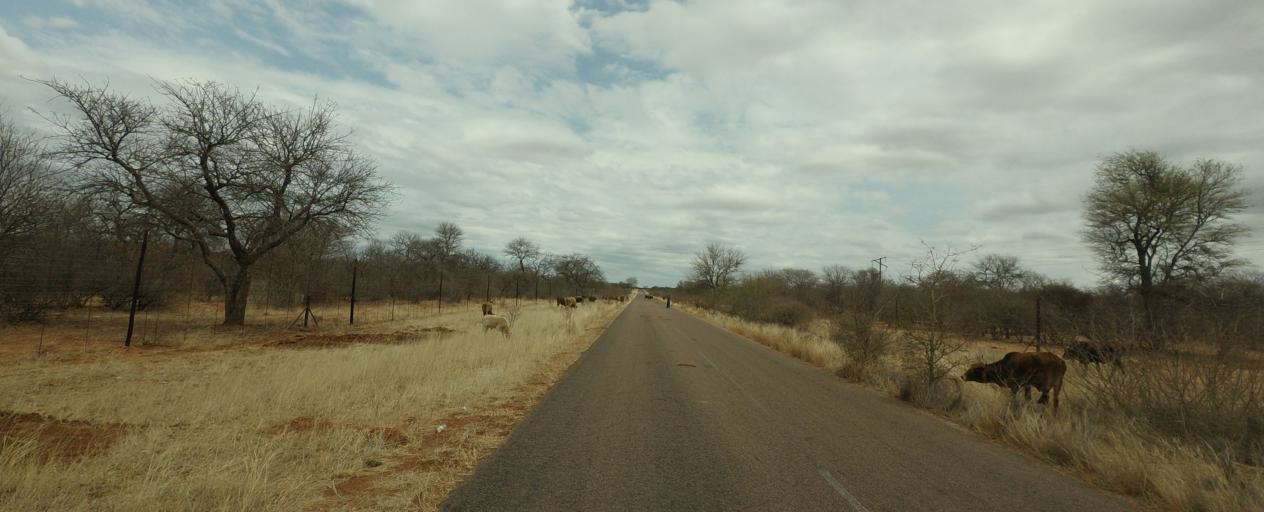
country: BW
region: Central
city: Mathathane
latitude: -22.6628
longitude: 28.7033
